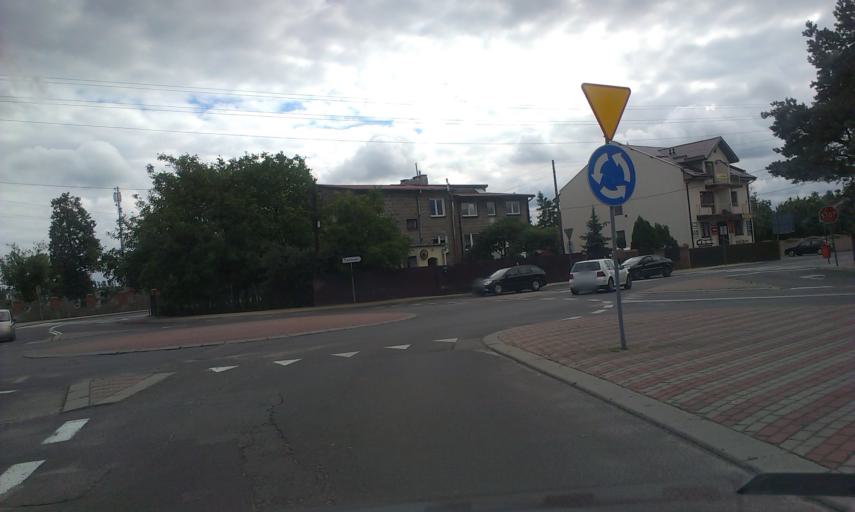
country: PL
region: Masovian Voivodeship
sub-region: Powiat zyrardowski
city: Mszczonow
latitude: 51.9742
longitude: 20.5274
